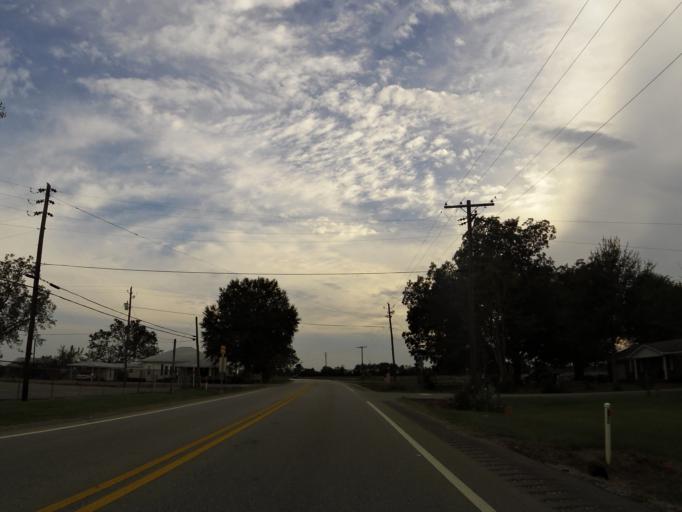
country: US
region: Alabama
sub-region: Monroe County
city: Frisco City
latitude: 31.3007
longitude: -87.5029
